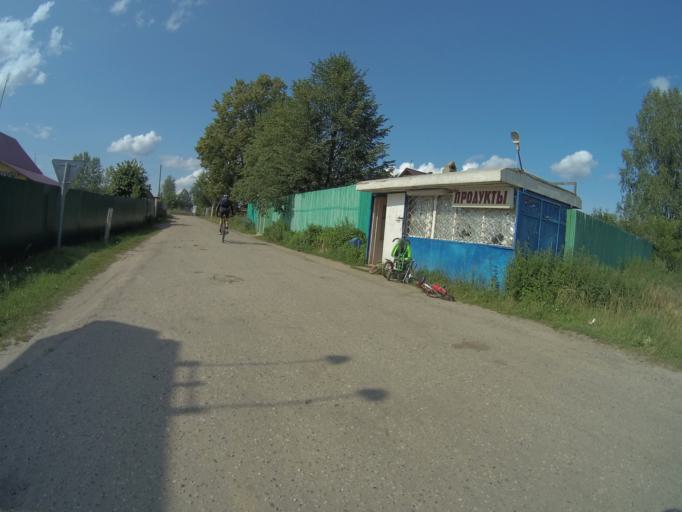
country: RU
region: Ivanovo
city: Novoye Leushino
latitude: 56.7160
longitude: 40.6671
